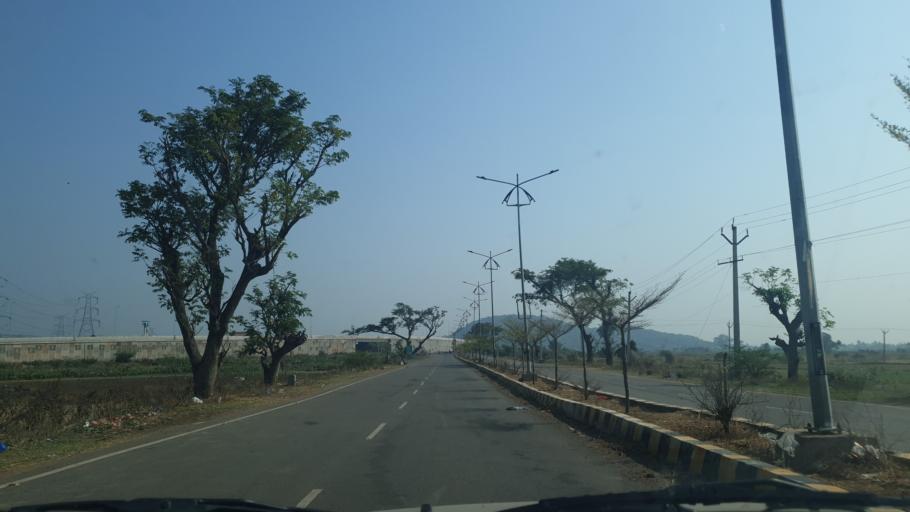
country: IN
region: Andhra Pradesh
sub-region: Srikakulam
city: Tekkali
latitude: 18.6167
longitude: 84.2405
